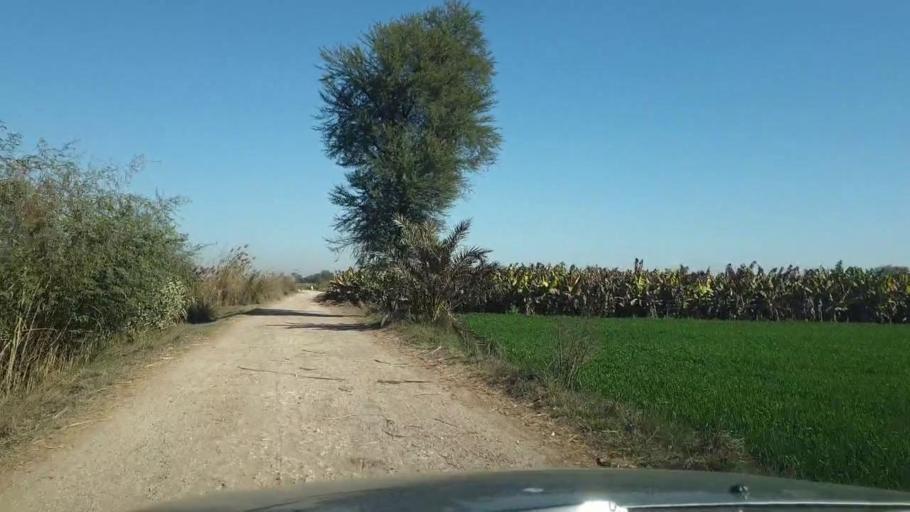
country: PK
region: Sindh
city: Ghotki
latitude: 28.0224
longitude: 69.2843
